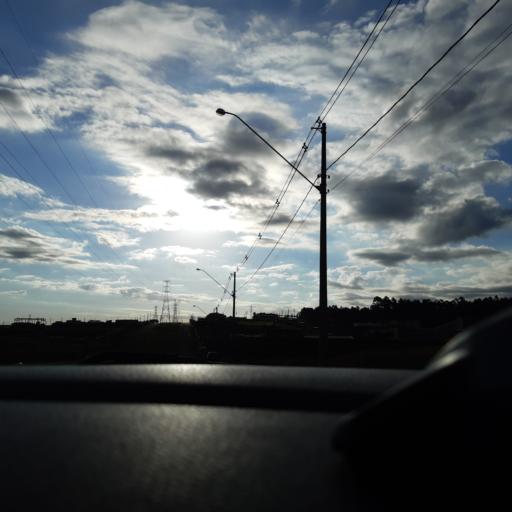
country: BR
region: Sao Paulo
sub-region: Ourinhos
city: Ourinhos
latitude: -22.9996
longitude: -49.8465
